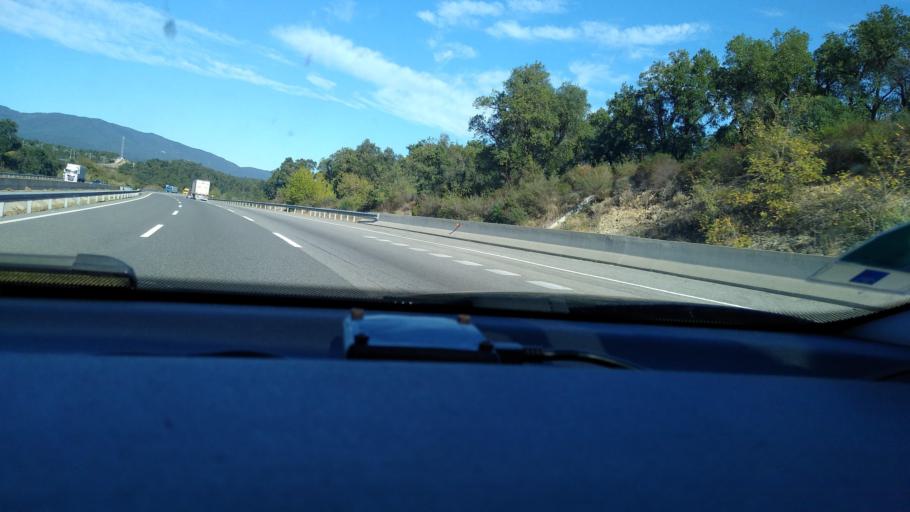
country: ES
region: Catalonia
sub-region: Provincia de Girona
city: Capmany
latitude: 42.3731
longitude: 2.8891
